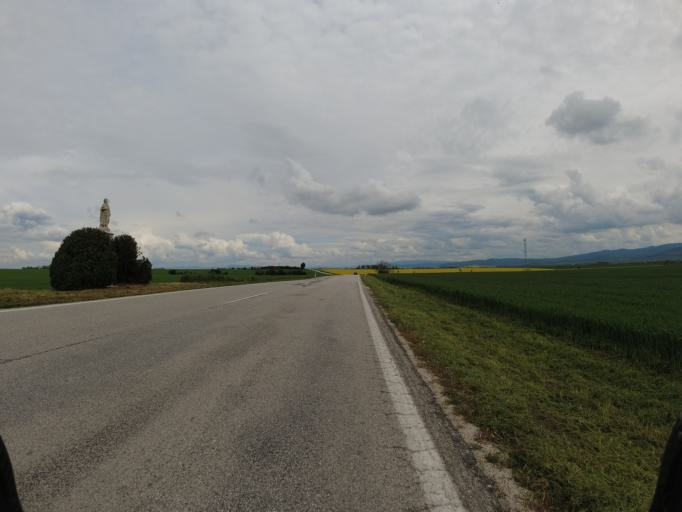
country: SK
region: Nitriansky
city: Banovce nad Bebravou
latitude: 48.5466
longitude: 18.1094
